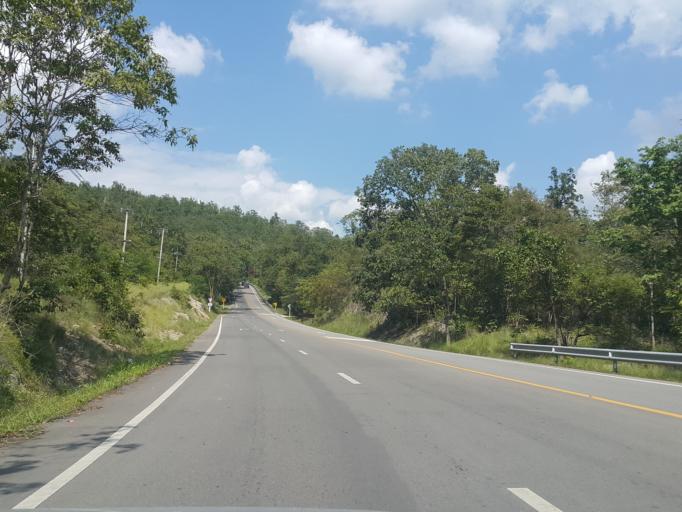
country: TH
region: Chiang Mai
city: Chom Thong
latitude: 18.4976
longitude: 98.6719
